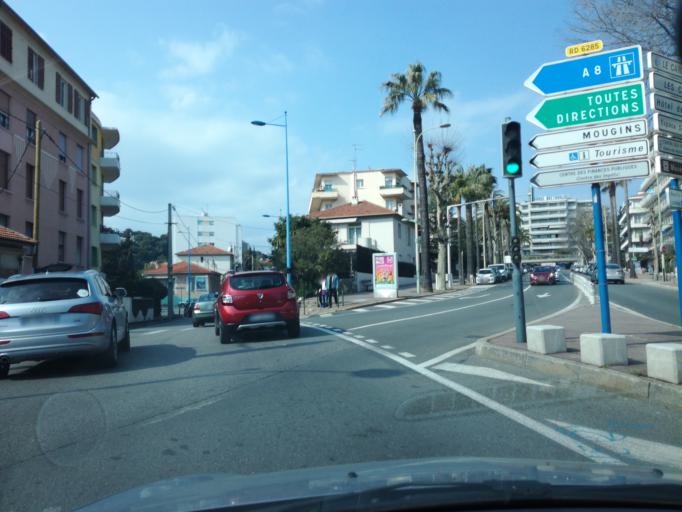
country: FR
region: Provence-Alpes-Cote d'Azur
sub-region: Departement des Alpes-Maritimes
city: Le Cannet
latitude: 43.5702
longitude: 7.0164
